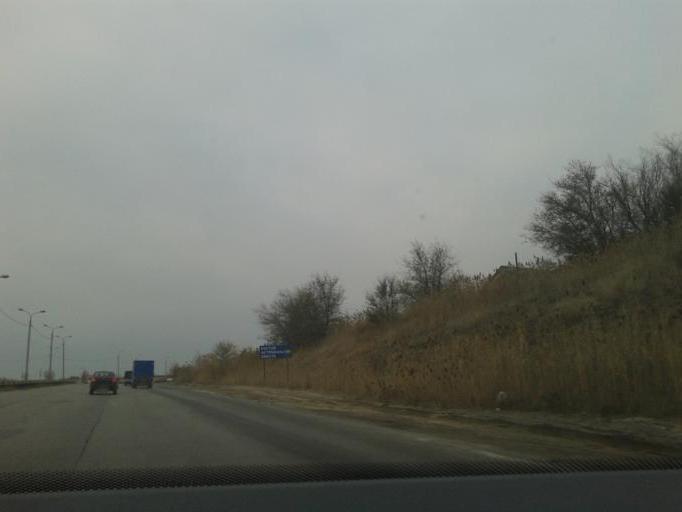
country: RU
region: Volgograd
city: Volgograd
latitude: 48.7081
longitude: 44.4416
